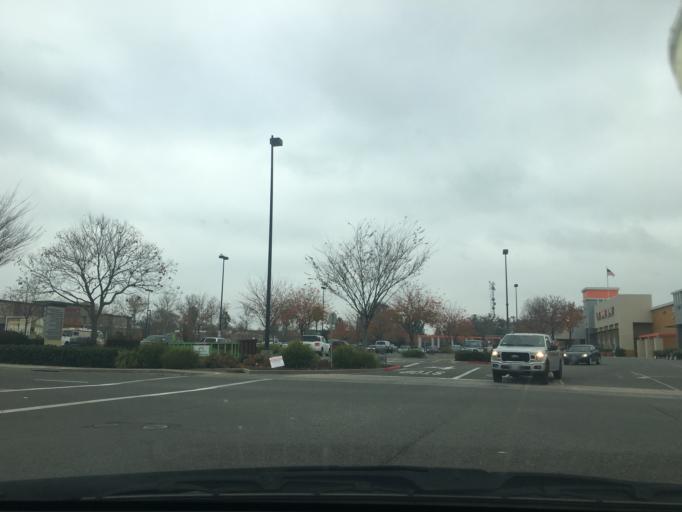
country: US
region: California
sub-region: Yolo County
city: West Sacramento
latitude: 38.5893
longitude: -121.5474
